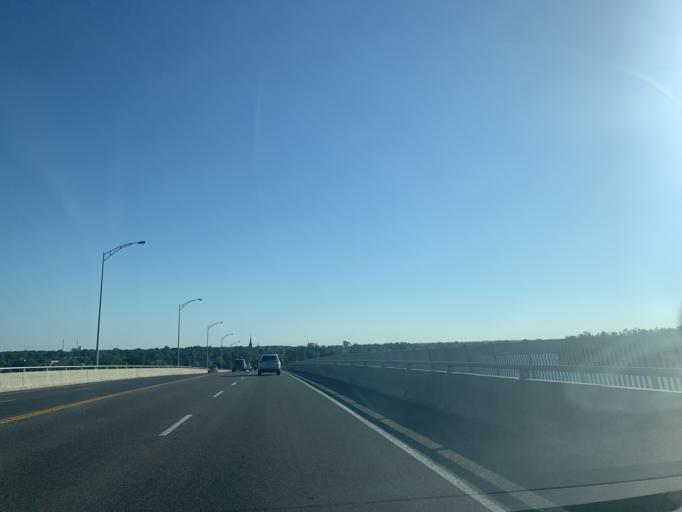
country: CA
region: Ontario
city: Hawkesbury
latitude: 45.6184
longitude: -74.5980
